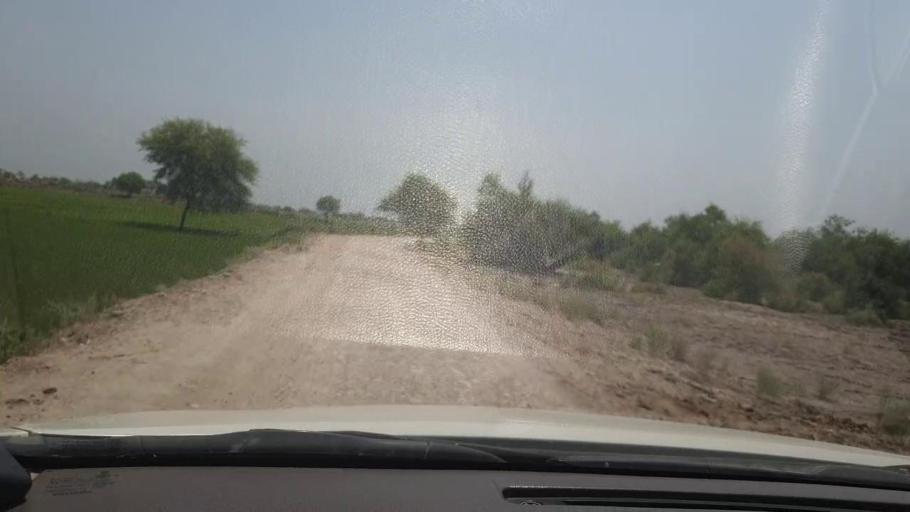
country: PK
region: Sindh
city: Garhi Yasin
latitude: 27.9199
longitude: 68.5535
